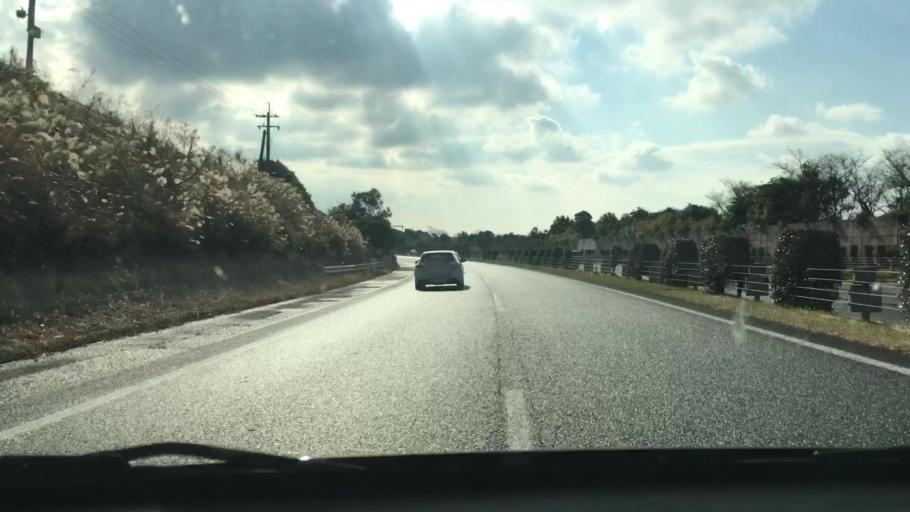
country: JP
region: Kumamoto
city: Yatsushiro
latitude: 32.5385
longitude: 130.6745
